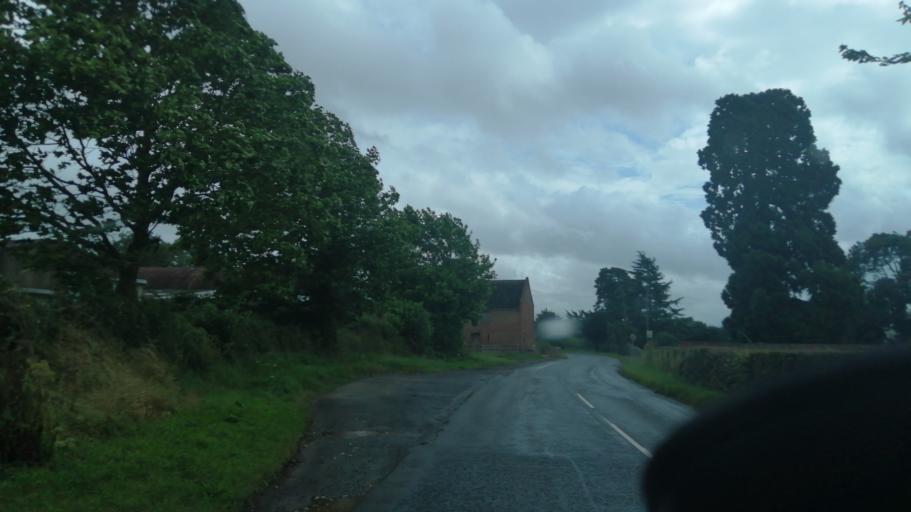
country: GB
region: England
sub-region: Herefordshire
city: Kingstone
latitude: 52.0175
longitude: -2.8474
